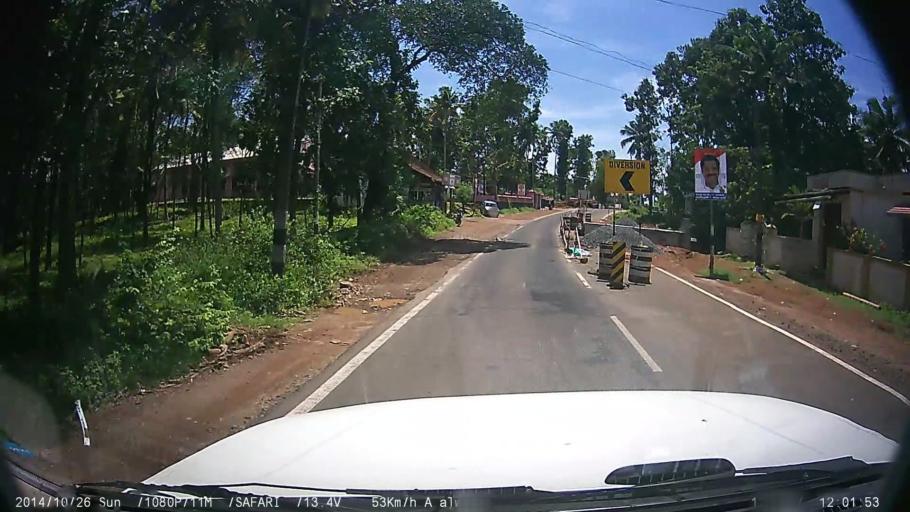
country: IN
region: Kerala
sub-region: Kottayam
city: Palackattumala
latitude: 9.6974
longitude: 76.5586
